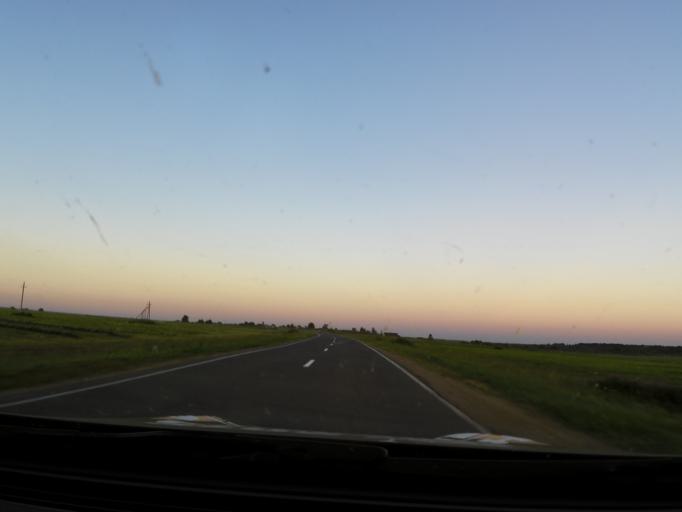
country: RU
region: Jaroslavl
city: Lyubim
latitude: 58.3193
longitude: 40.9279
